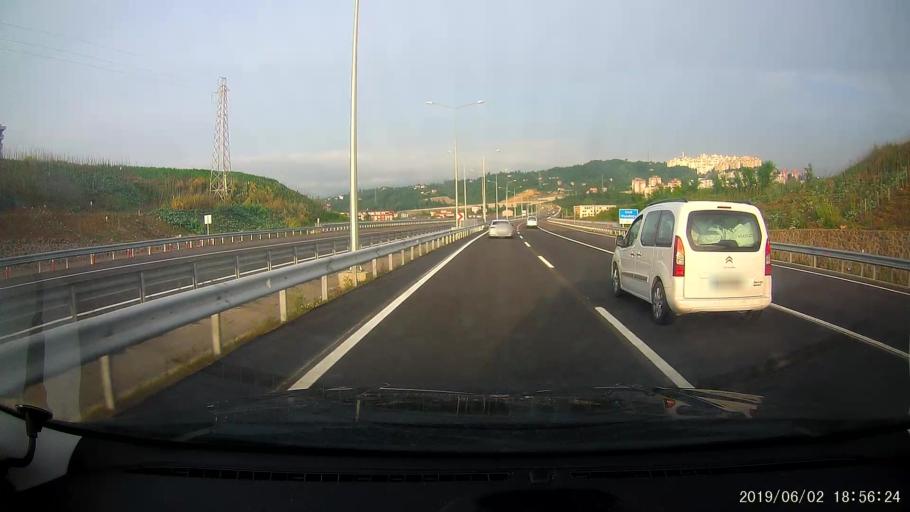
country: TR
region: Ordu
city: Ordu
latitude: 40.9560
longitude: 37.8900
